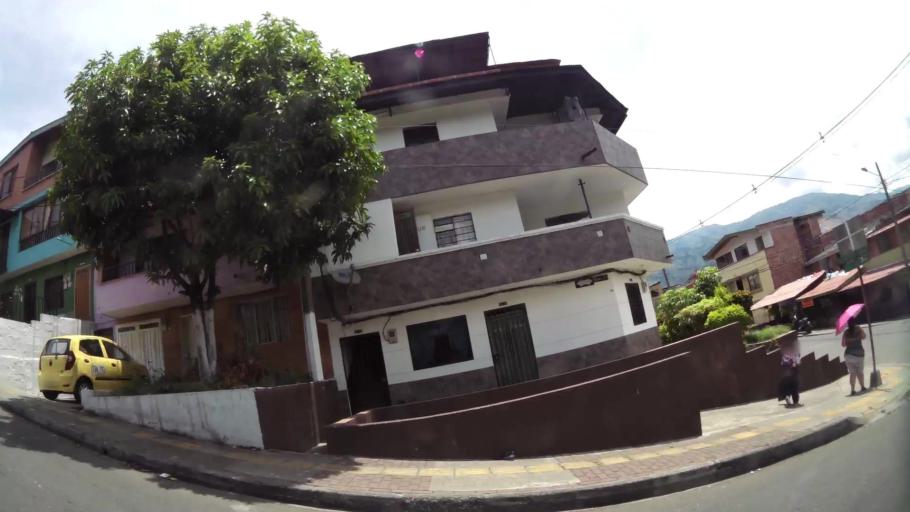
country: CO
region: Antioquia
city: Bello
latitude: 6.3426
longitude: -75.5559
